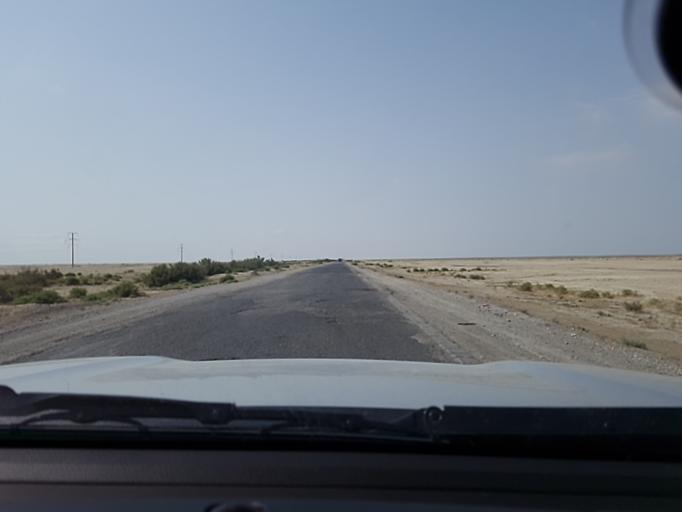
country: TM
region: Balkan
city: Gumdag
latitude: 38.9812
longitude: 54.5873
